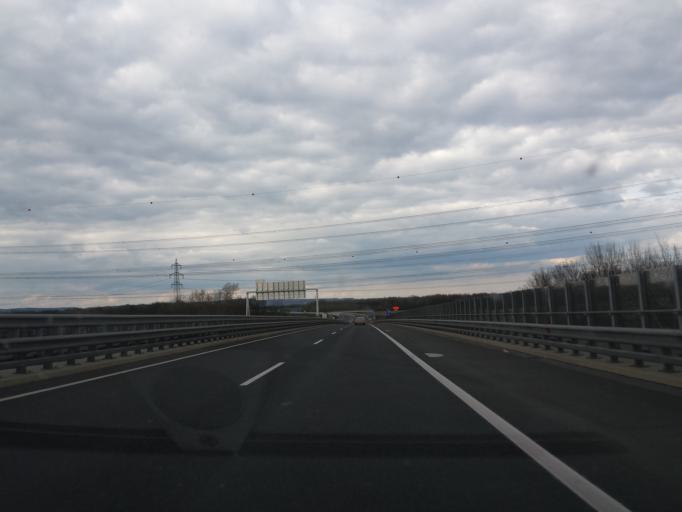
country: AT
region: Lower Austria
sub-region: Politischer Bezirk Krems
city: Grafenegg
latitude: 48.3868
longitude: 15.7240
